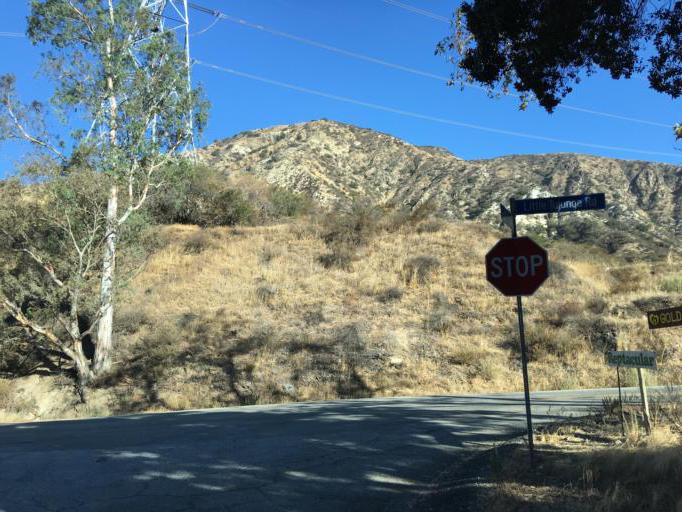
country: US
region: California
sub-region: Los Angeles County
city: San Fernando
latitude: 34.3170
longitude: -118.3411
